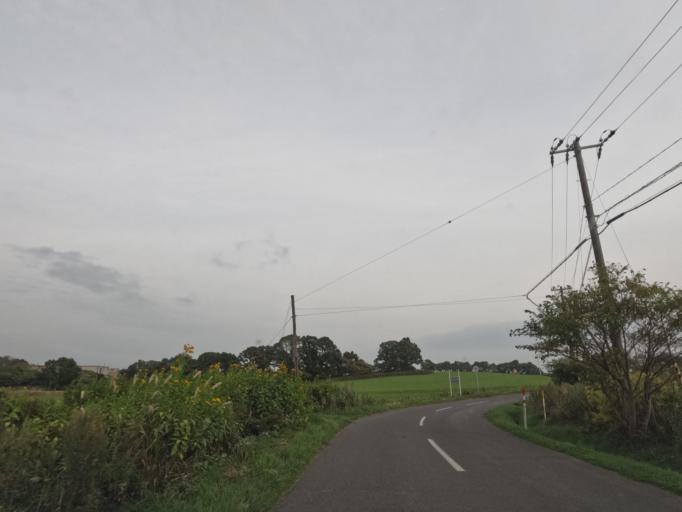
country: JP
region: Hokkaido
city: Date
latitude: 42.4088
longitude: 140.9199
